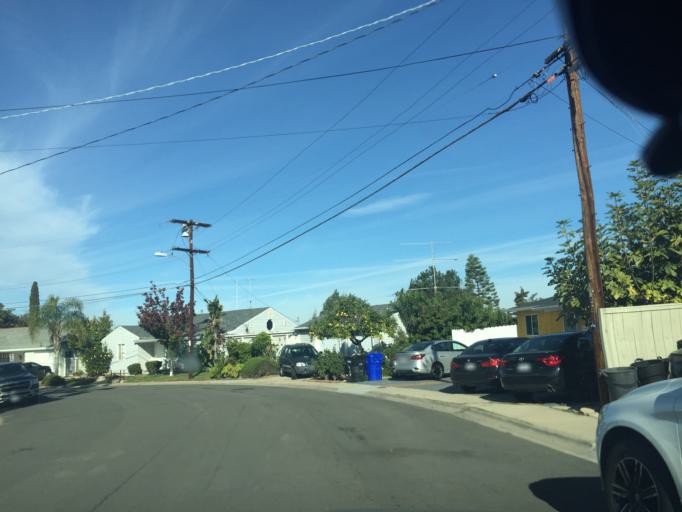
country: US
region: California
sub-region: San Diego County
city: Lemon Grove
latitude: 32.7664
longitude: -117.0812
